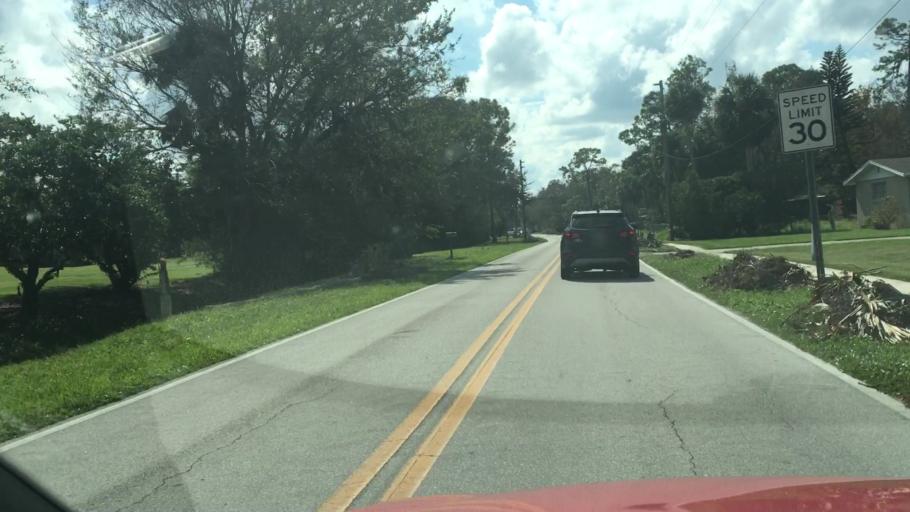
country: US
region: Florida
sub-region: Volusia County
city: Ormond Beach
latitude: 29.2594
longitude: -81.0607
